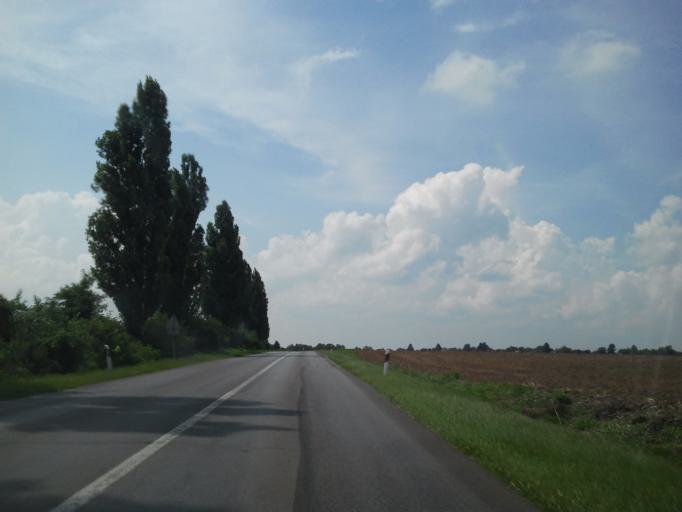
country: HR
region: Osjecko-Baranjska
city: Dalj
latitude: 45.5161
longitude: 18.9197
